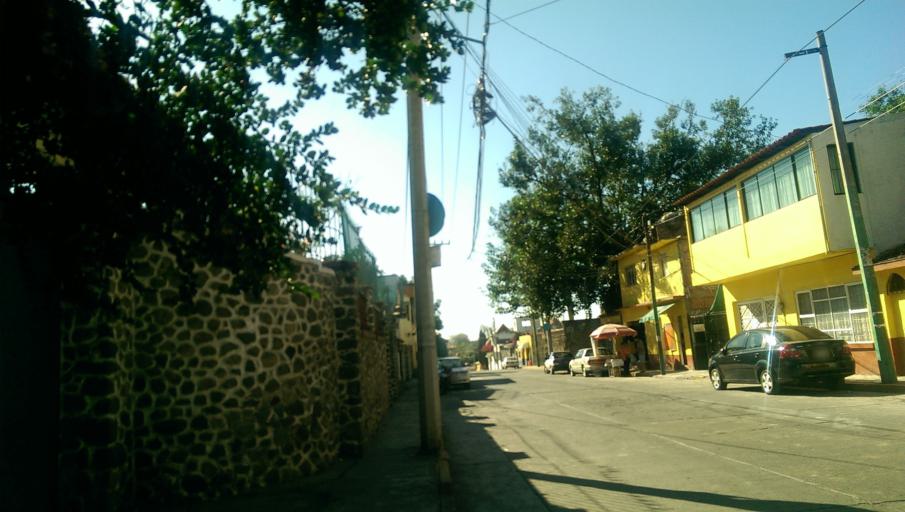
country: MX
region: Morelos
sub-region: Cuernavaca
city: Cuernavaca
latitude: 18.9207
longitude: -99.2415
